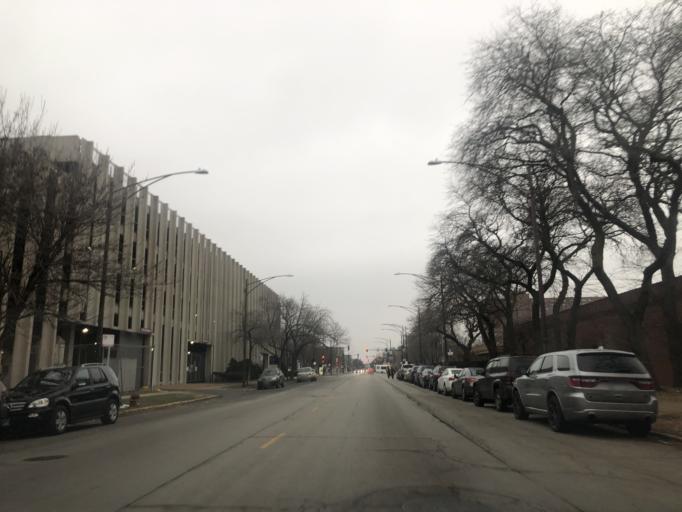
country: US
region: Illinois
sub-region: Cook County
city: Chicago
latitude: 41.7890
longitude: -87.6061
